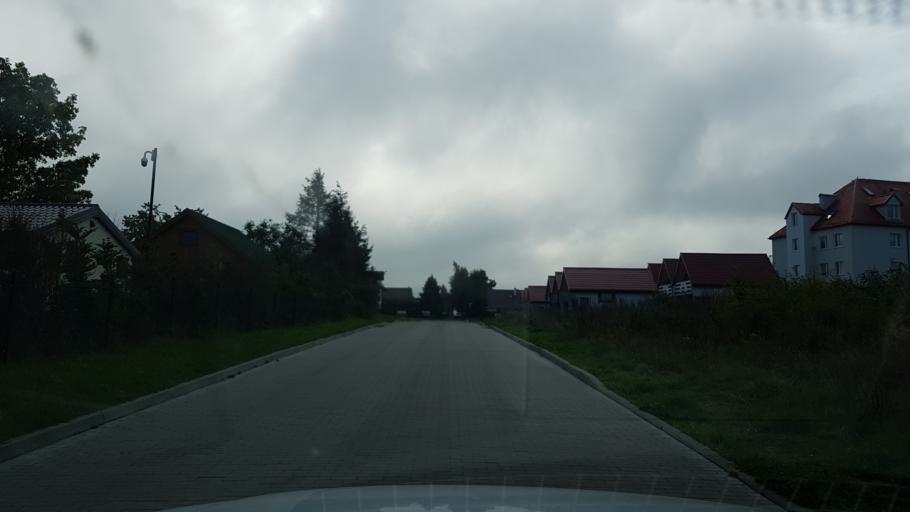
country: PL
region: West Pomeranian Voivodeship
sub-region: Powiat kolobrzeski
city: Ustronie Morskie
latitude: 54.2134
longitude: 15.7551
